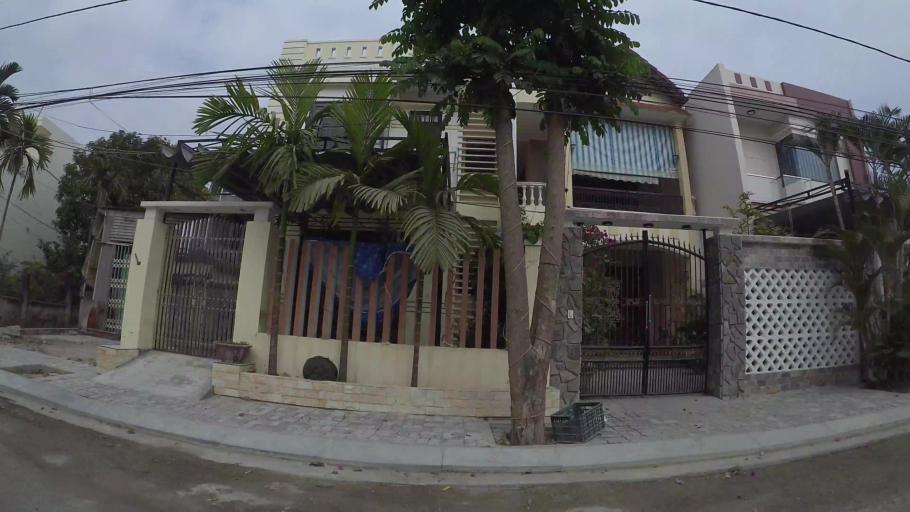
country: VN
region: Da Nang
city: Son Tra
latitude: 16.0642
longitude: 108.2408
